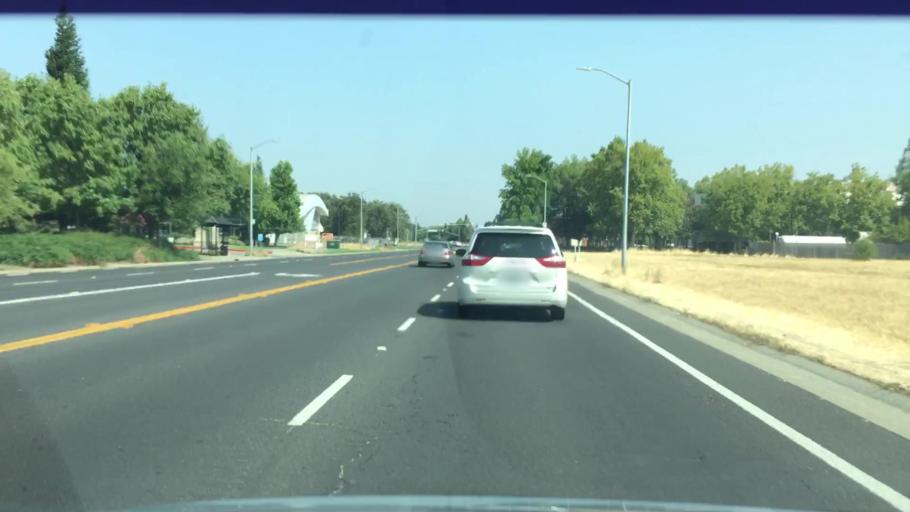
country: US
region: California
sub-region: Sacramento County
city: Laguna
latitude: 38.4192
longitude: -121.4063
